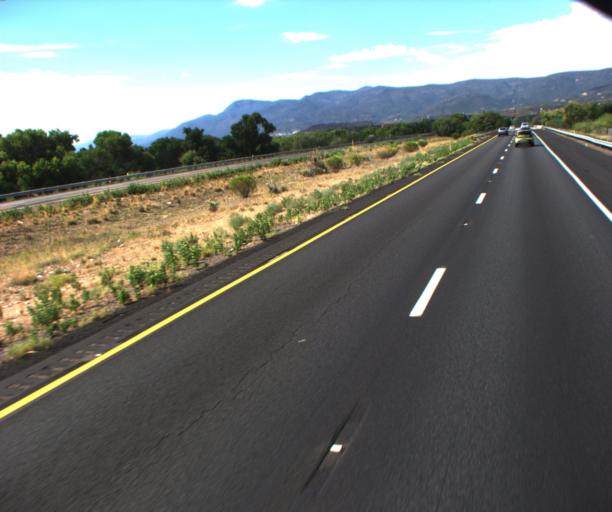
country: US
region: Arizona
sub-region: Yavapai County
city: Camp Verde
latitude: 34.5892
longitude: -111.8783
